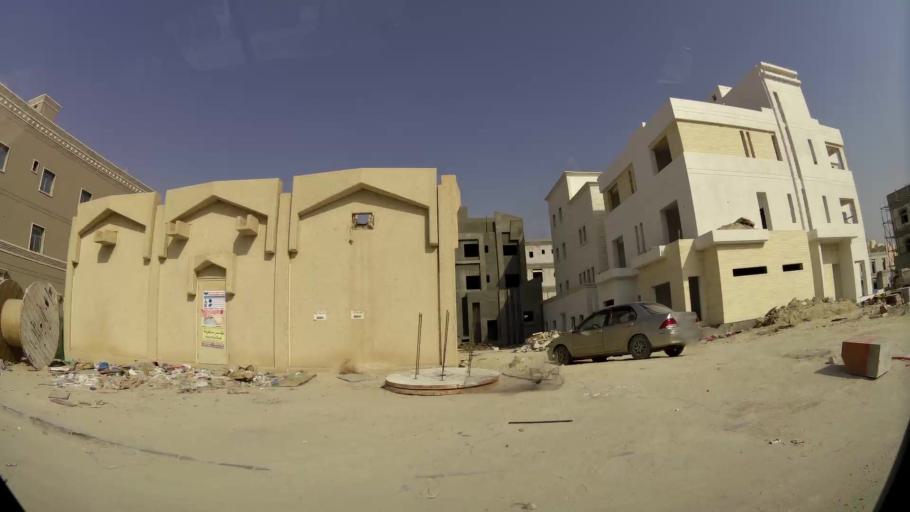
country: KW
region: Muhafazat al Jahra'
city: Al Jahra'
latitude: 29.3495
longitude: 47.7436
